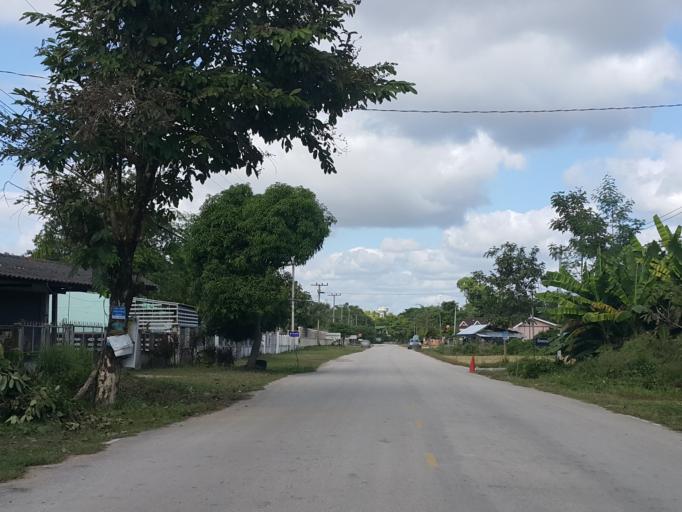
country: TH
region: Lampang
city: Hang Chat
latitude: 18.3334
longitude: 99.3548
